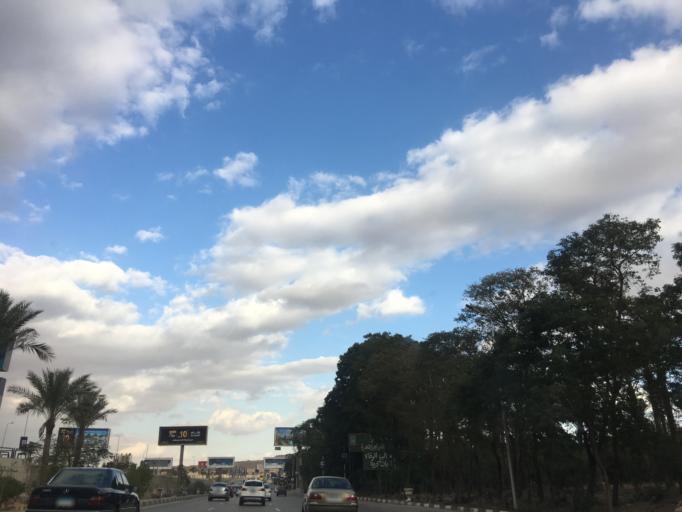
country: EG
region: Muhafazat al Qahirah
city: Cairo
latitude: 30.0231
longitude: 31.3546
